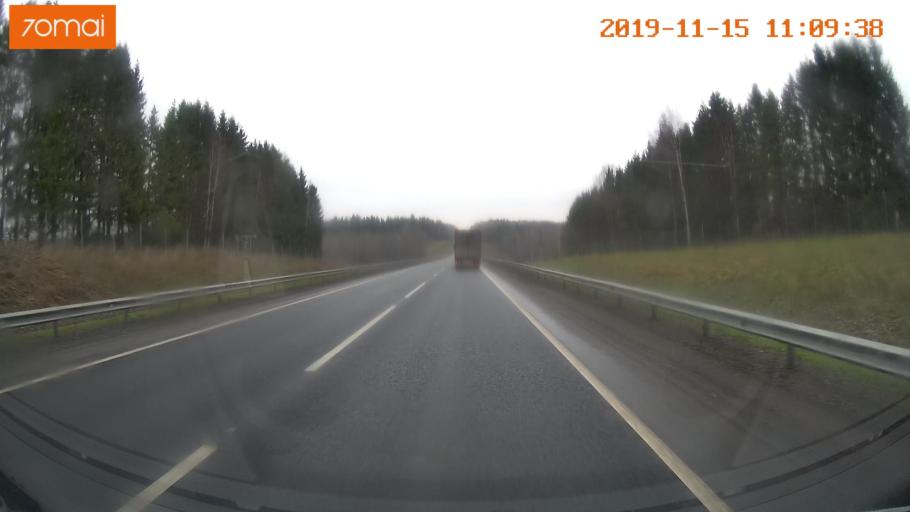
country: RU
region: Vologda
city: Chebsara
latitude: 59.1205
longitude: 39.1028
